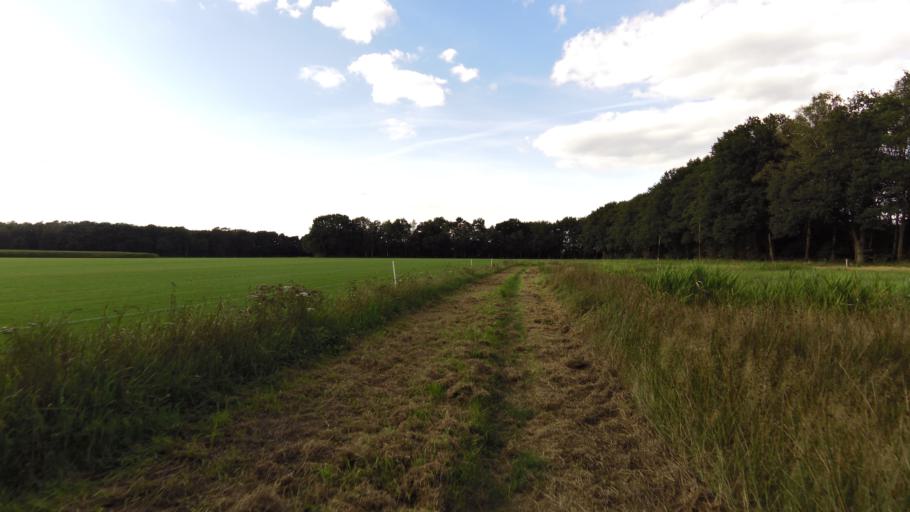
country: NL
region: Gelderland
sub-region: Gemeente Apeldoorn
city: Uddel
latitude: 52.2492
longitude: 5.7809
